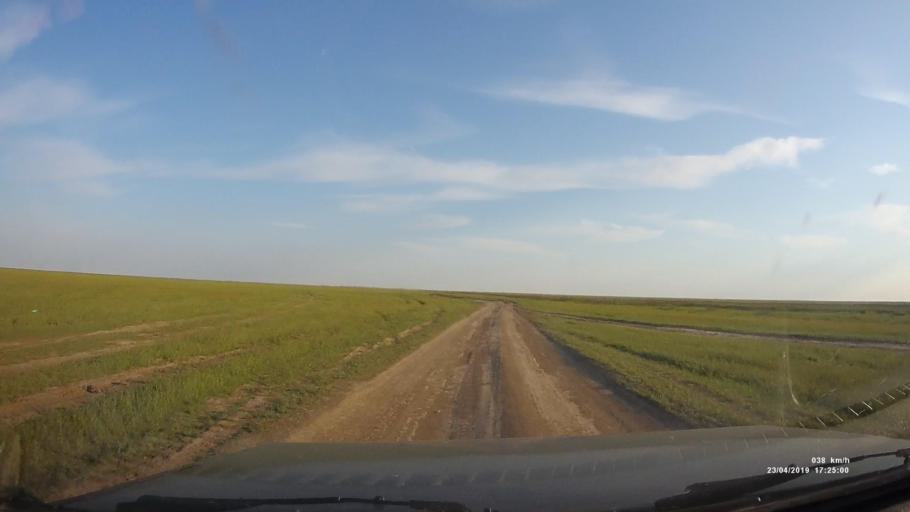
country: RU
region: Kalmykiya
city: Priyutnoye
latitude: 46.1547
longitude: 43.5095
